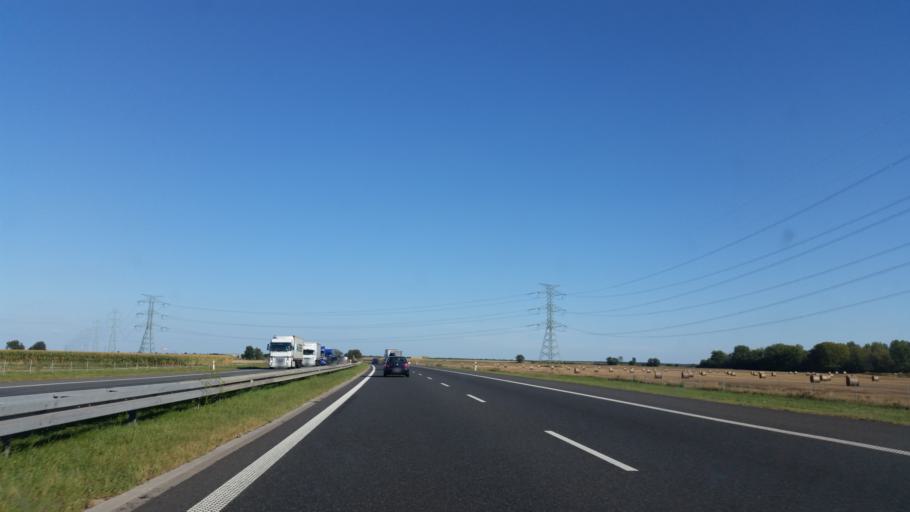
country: PL
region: Opole Voivodeship
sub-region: Powiat brzeski
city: Olszanka
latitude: 50.7443
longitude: 17.4535
